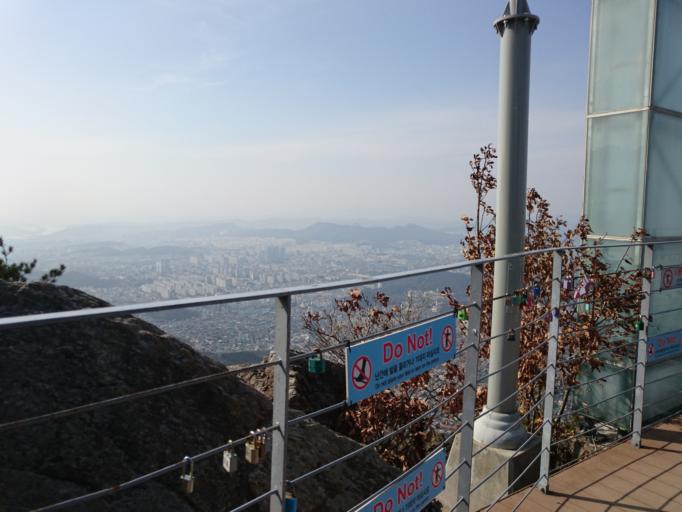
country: KR
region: Daegu
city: Daegu
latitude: 35.8247
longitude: 128.5795
